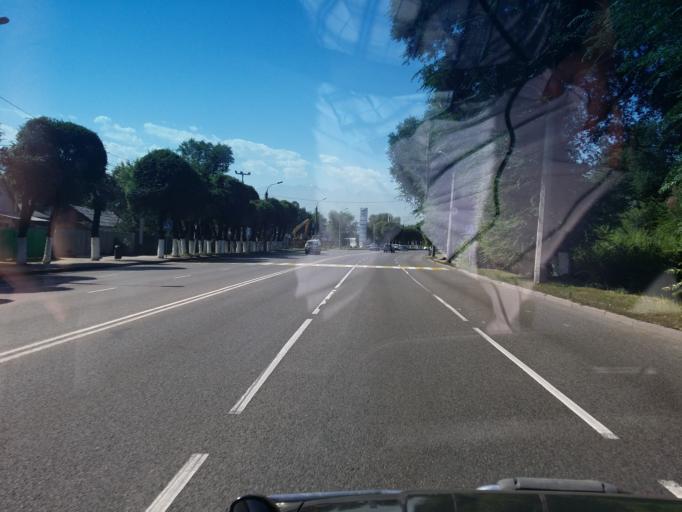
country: KZ
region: Almaty Qalasy
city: Almaty
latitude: 43.3004
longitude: 76.9514
